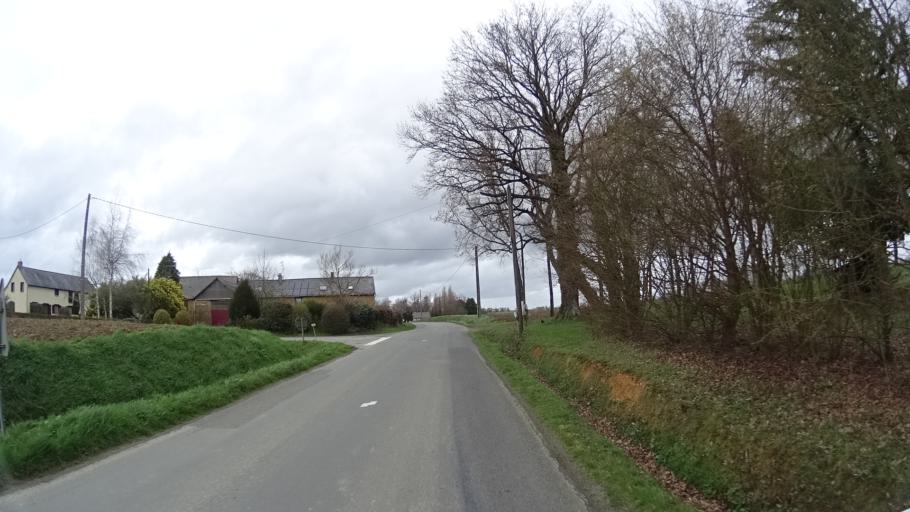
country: FR
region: Brittany
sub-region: Departement d'Ille-et-Vilaine
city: Saint-Gilles
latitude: 48.1975
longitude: -1.8309
